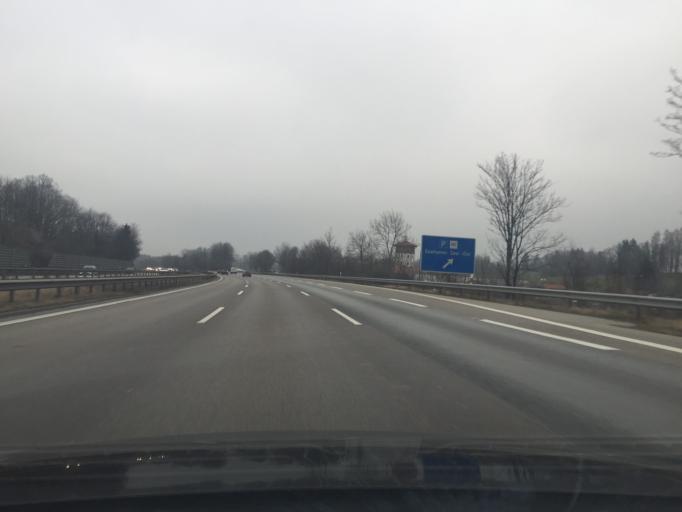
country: DE
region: Bavaria
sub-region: Upper Bavaria
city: Vagen
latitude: 47.8545
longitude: 11.8606
